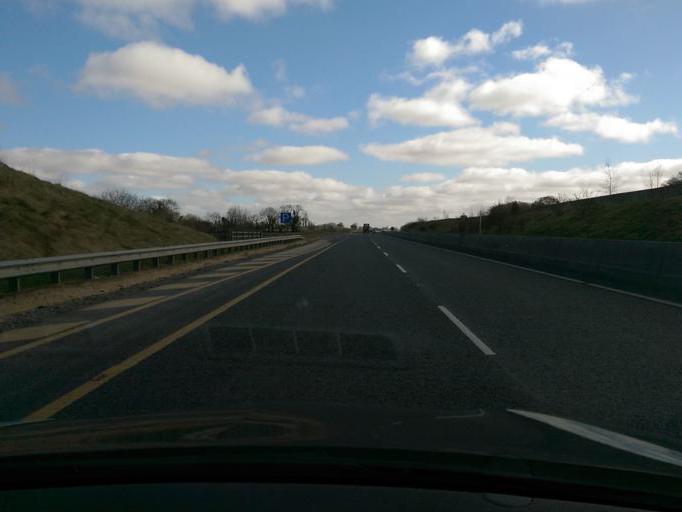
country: IE
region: Leinster
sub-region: An Iarmhi
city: Kilbeggan
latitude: 53.3593
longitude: -7.4471
